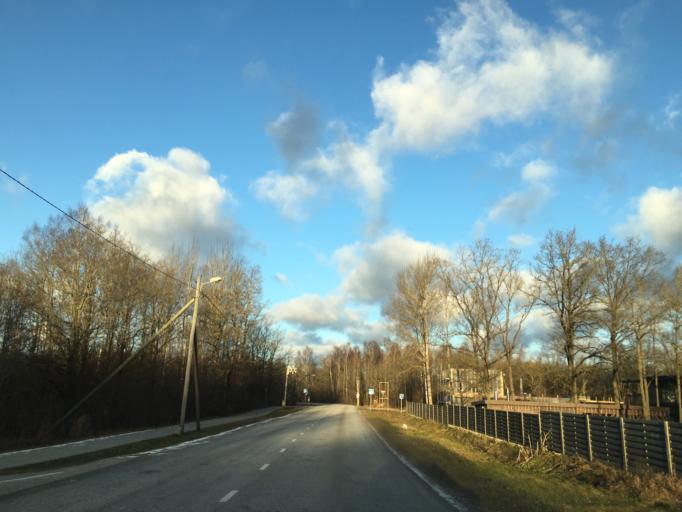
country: EE
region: Harju
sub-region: Saue linn
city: Saue
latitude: 59.3158
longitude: 24.5595
